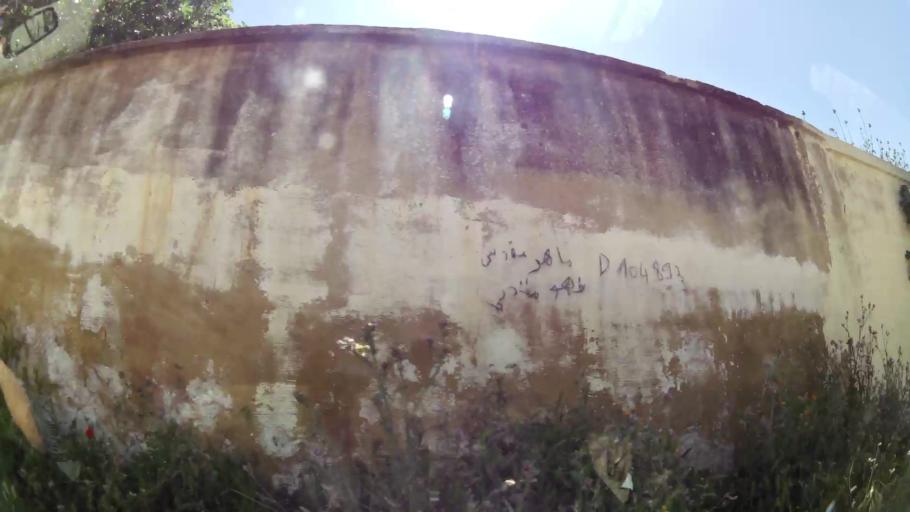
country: MA
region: Meknes-Tafilalet
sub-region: Meknes
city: Meknes
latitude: 33.8876
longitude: -5.5454
